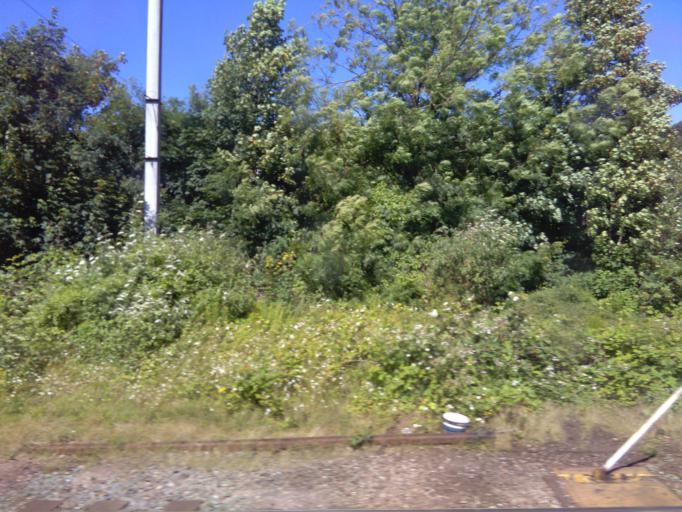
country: GB
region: England
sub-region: Luton
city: Luton
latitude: 51.8802
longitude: -0.4063
